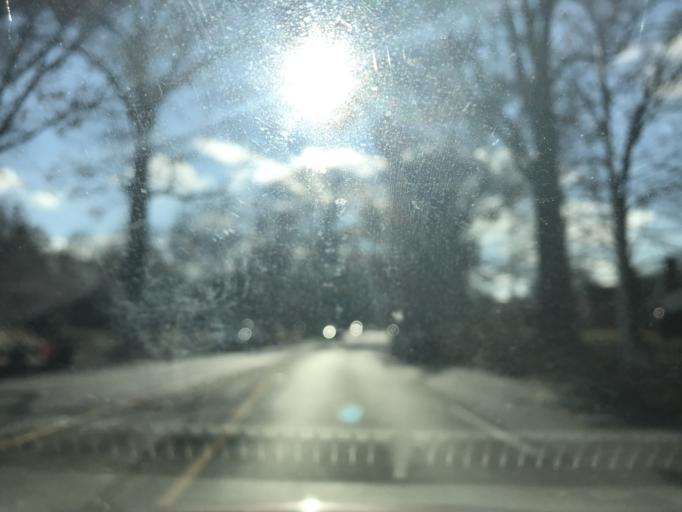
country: US
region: Kentucky
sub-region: Jefferson County
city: Audubon Park
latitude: 38.2229
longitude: -85.7310
